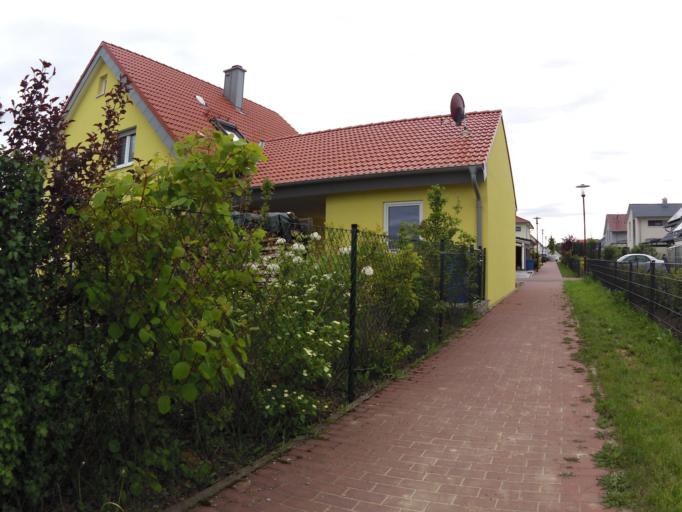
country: DE
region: Bavaria
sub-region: Regierungsbezirk Unterfranken
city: Kurnach
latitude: 49.8492
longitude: 10.0528
